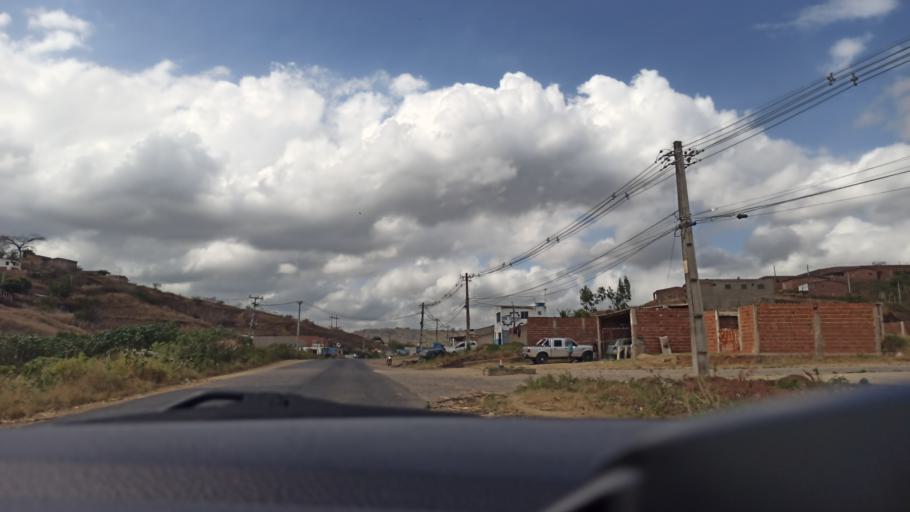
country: BR
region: Pernambuco
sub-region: Timbauba
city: Timbauba
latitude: -7.5028
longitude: -35.2990
